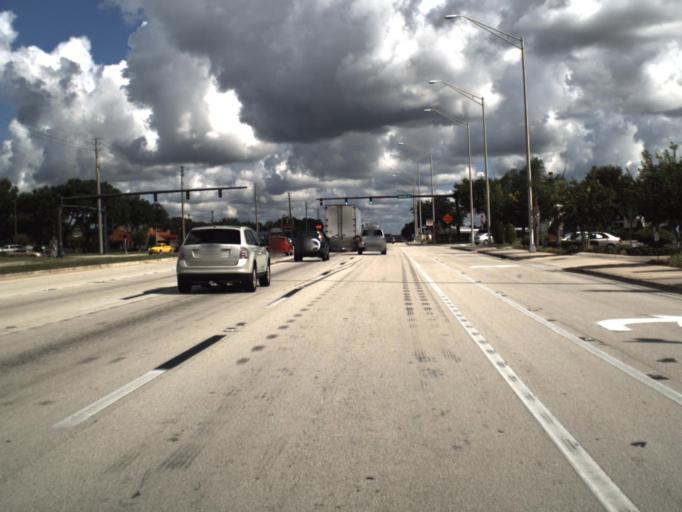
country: US
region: Florida
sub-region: Polk County
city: Gibsonia
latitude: 28.1197
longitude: -81.9735
